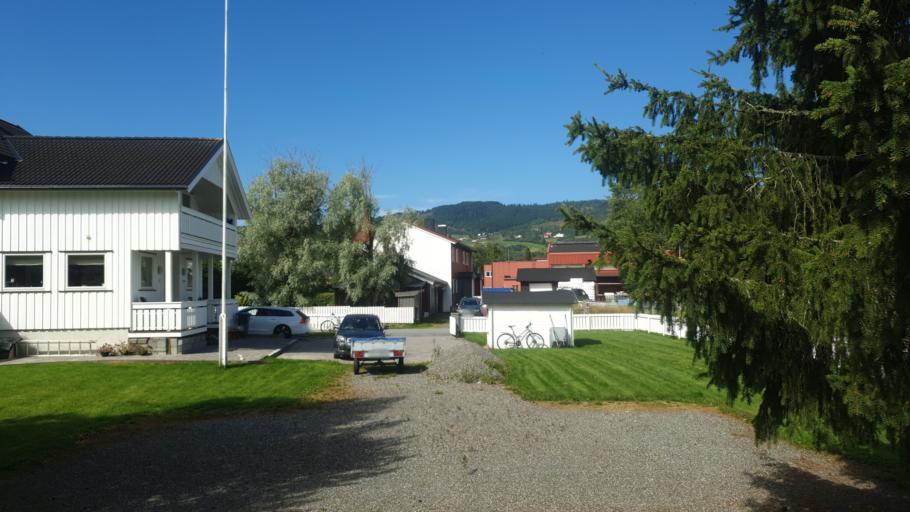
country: NO
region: Sor-Trondelag
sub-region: Orkdal
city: Orkanger
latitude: 63.2760
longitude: 9.8238
